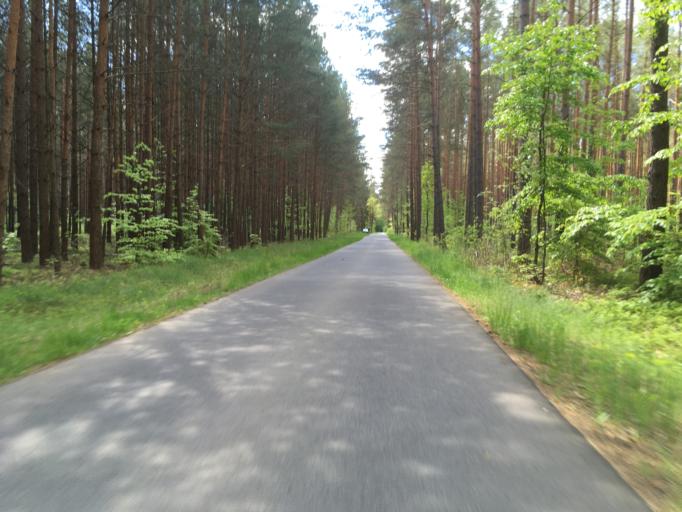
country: DE
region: Brandenburg
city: Templin
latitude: 53.0028
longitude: 13.5632
